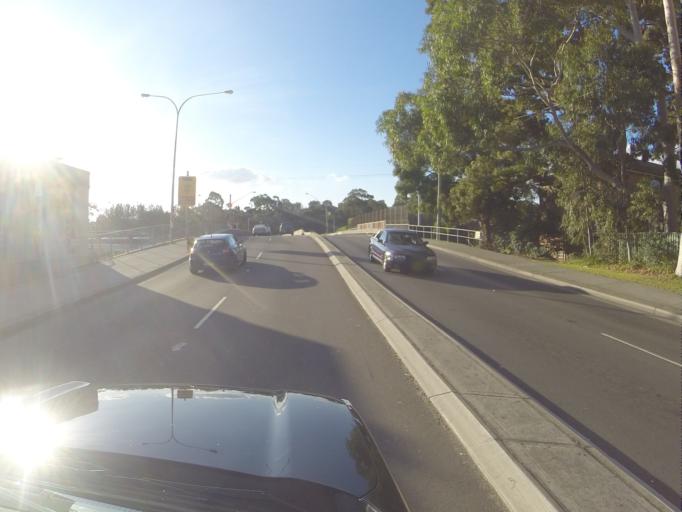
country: AU
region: New South Wales
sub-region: Rockdale
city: Bexley North
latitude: -33.9380
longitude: 151.1141
